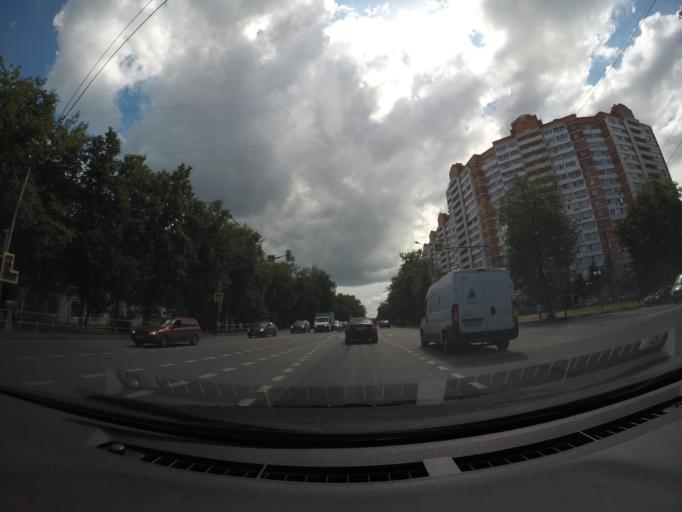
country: RU
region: Moscow
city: Zhulebino
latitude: 55.6938
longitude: 37.8643
